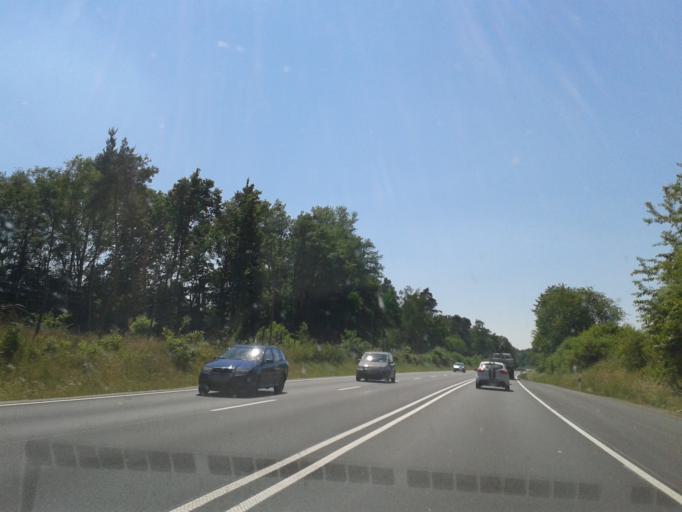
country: DE
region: North Rhine-Westphalia
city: Bad Lippspringe
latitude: 51.7842
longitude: 8.7895
